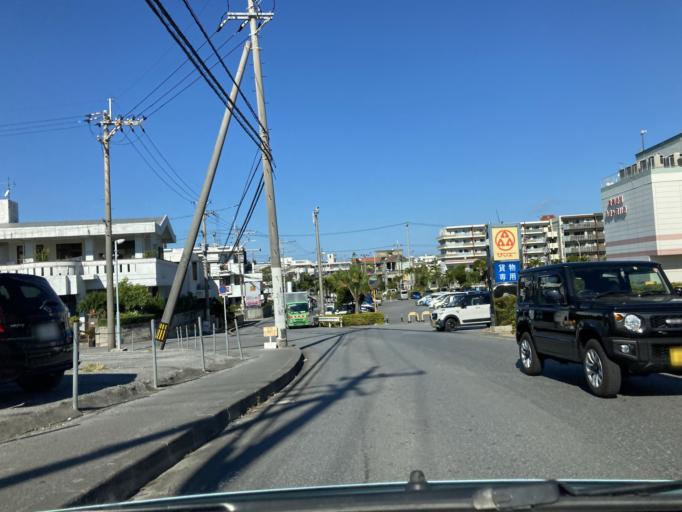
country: JP
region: Okinawa
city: Okinawa
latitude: 26.3525
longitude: 127.8246
